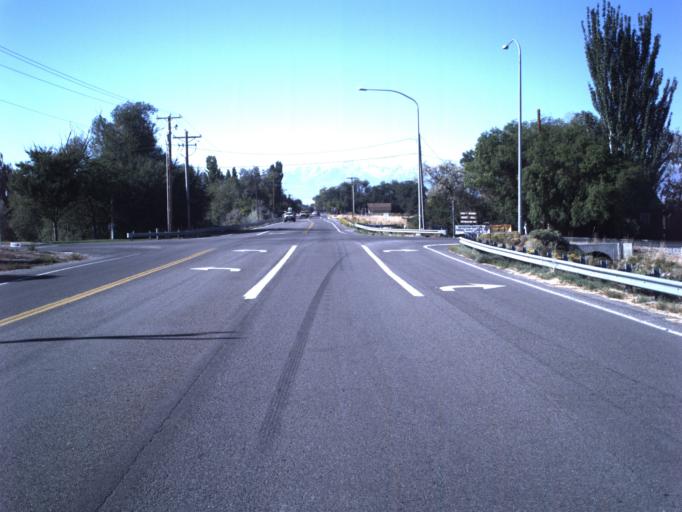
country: US
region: Utah
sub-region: Tooele County
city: Stansbury park
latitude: 40.6512
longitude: -112.2958
